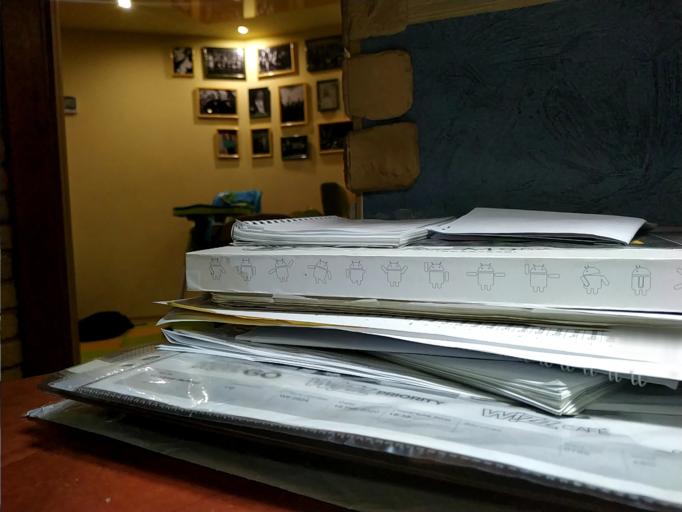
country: RU
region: Arkhangelskaya
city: Kargopol'
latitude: 61.5787
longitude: 39.2770
